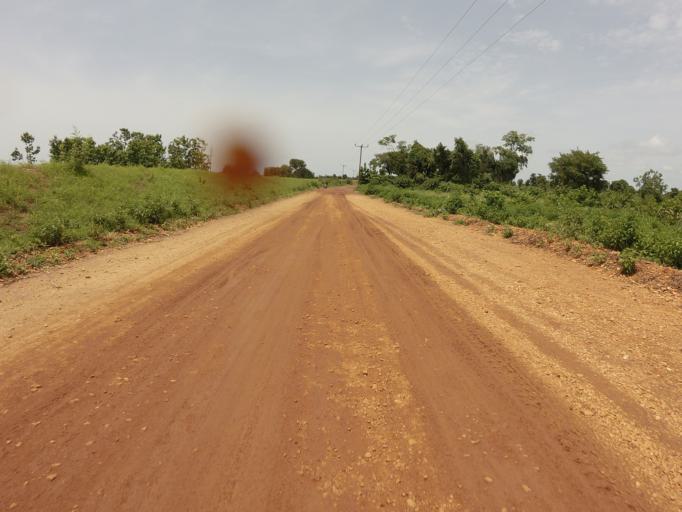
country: GH
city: Kpandae
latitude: 8.7165
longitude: 0.1432
